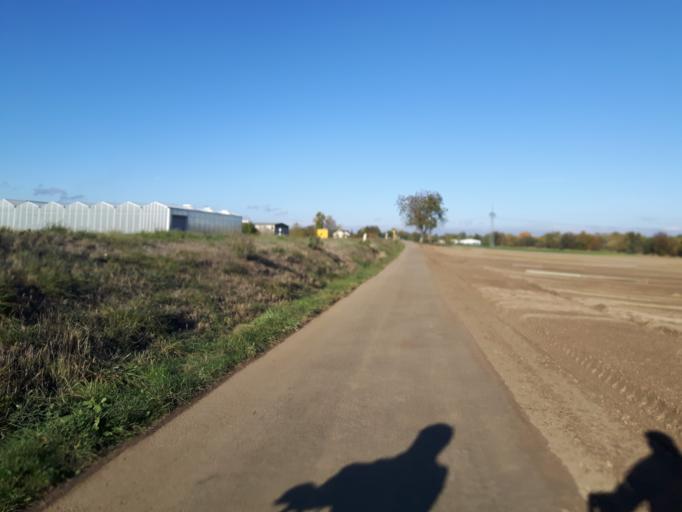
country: DE
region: Rheinland-Pfalz
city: Mutterstadt
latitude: 49.4128
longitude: 8.3345
